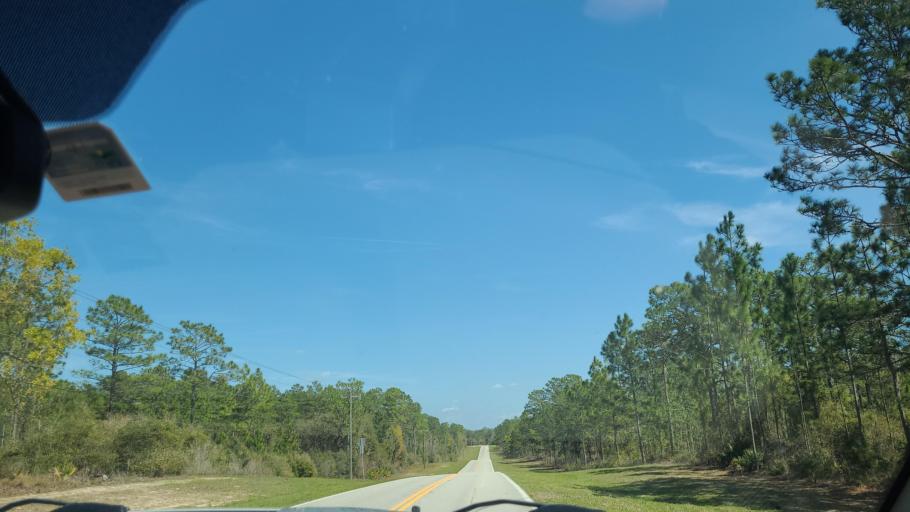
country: US
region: Florida
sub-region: Putnam County
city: Interlachen
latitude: 29.3664
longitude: -81.8181
